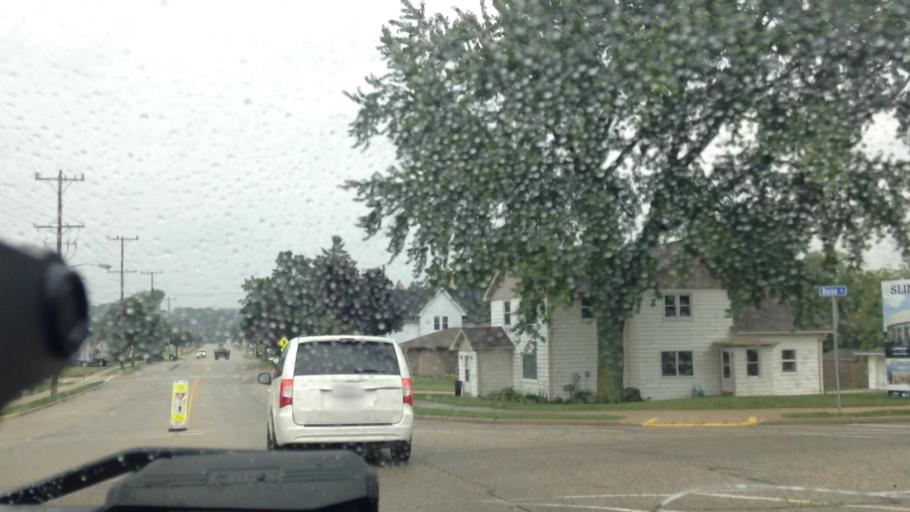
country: US
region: Wisconsin
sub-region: Washington County
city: Slinger
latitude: 43.3328
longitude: -88.2834
